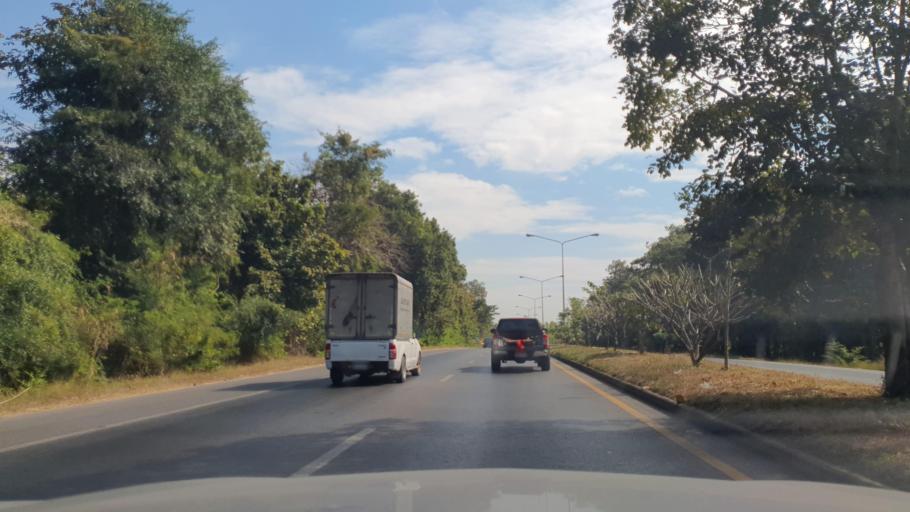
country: TH
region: Kalasin
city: Yang Talat
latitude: 16.4059
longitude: 103.4201
